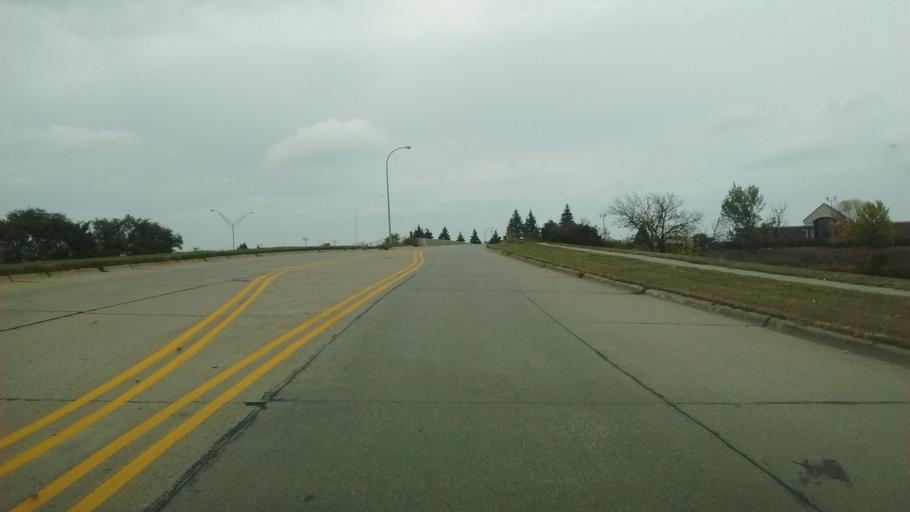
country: US
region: Iowa
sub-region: Woodbury County
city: Sergeant Bluff
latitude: 42.4424
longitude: -96.3525
